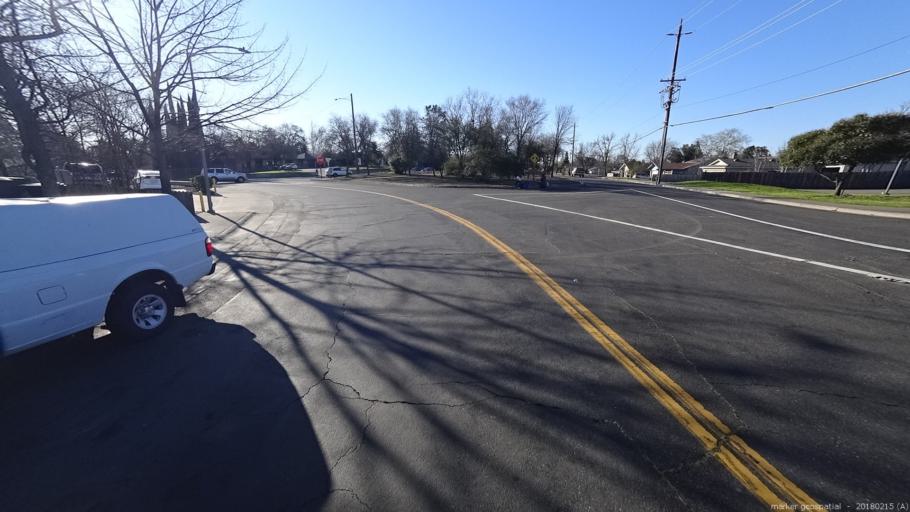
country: US
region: California
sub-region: Sacramento County
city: Foothill Farms
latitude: 38.6788
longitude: -121.3363
